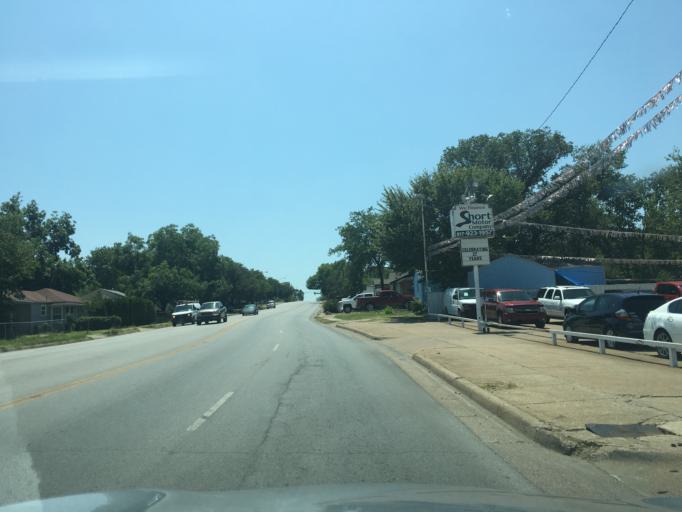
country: US
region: Texas
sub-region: Tarrant County
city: Edgecliff Village
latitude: 32.6843
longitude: -97.3531
